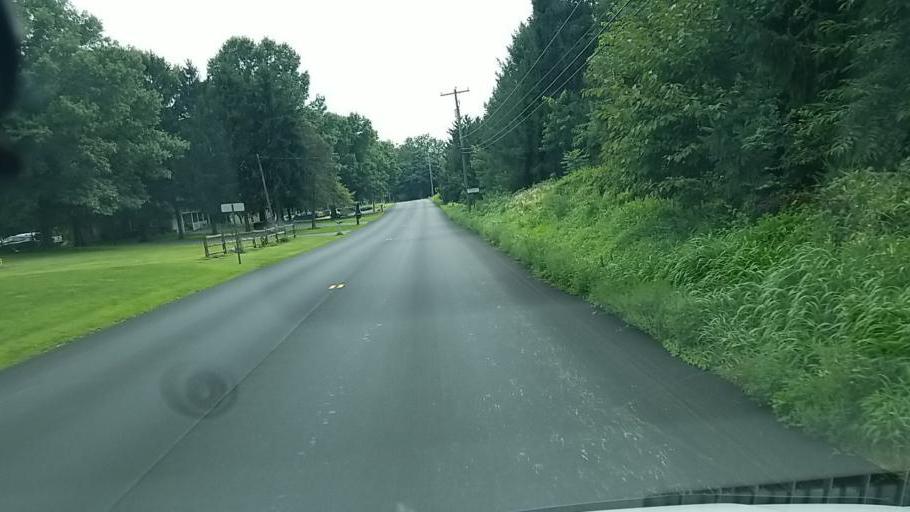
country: US
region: Pennsylvania
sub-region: Dauphin County
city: Elizabethville
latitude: 40.5840
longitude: -76.8149
